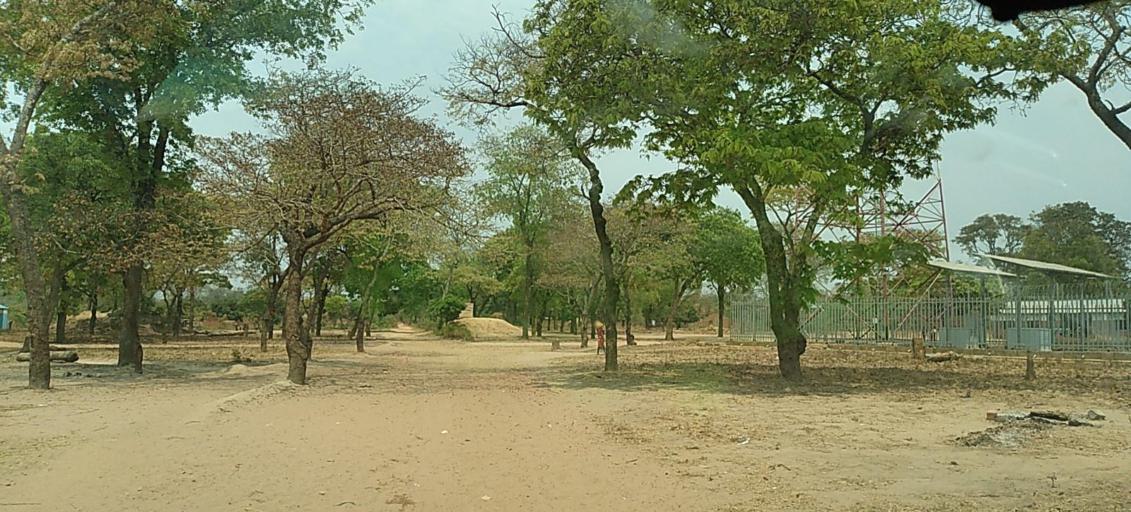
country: ZM
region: North-Western
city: Kabompo
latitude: -13.5700
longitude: 24.4411
